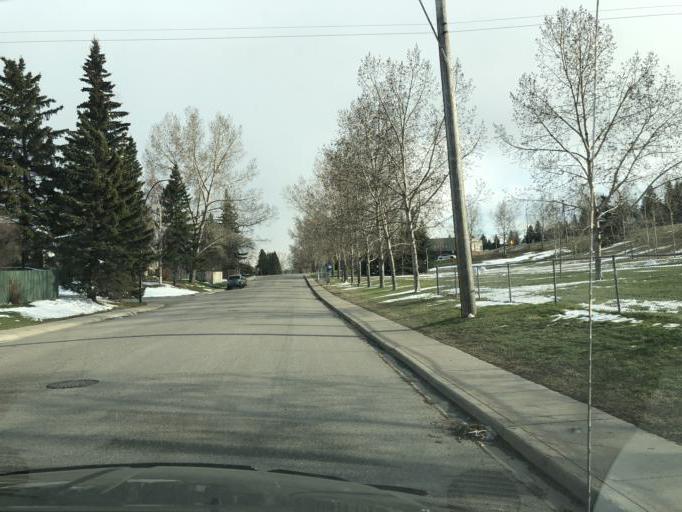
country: CA
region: Alberta
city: Calgary
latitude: 50.9438
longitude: -114.0340
